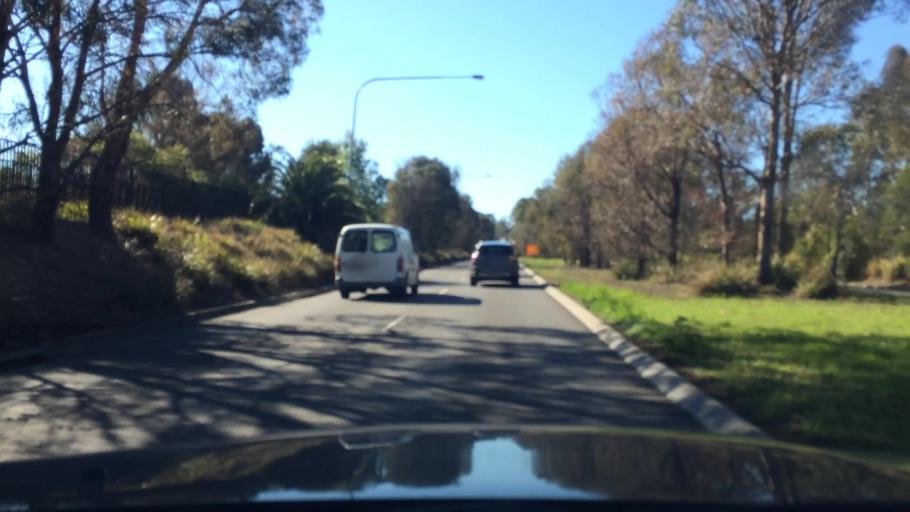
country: AU
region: New South Wales
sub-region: Fairfield
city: Cecil Park
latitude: -33.8930
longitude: 150.8578
